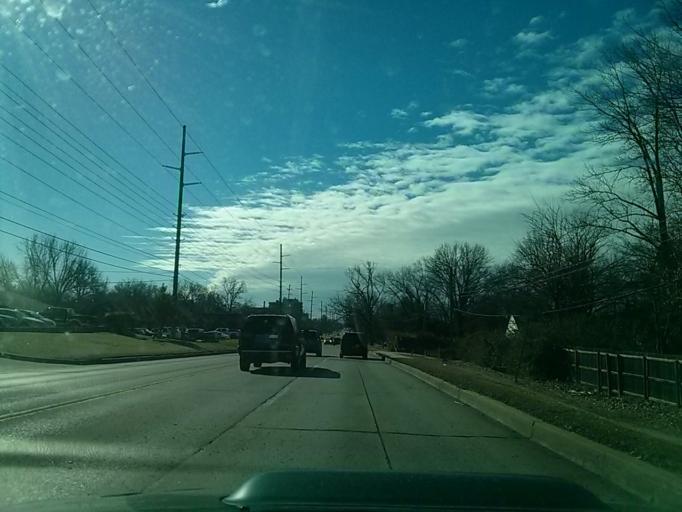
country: US
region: Oklahoma
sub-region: Tulsa County
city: Jenks
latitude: 36.0858
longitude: -95.9581
